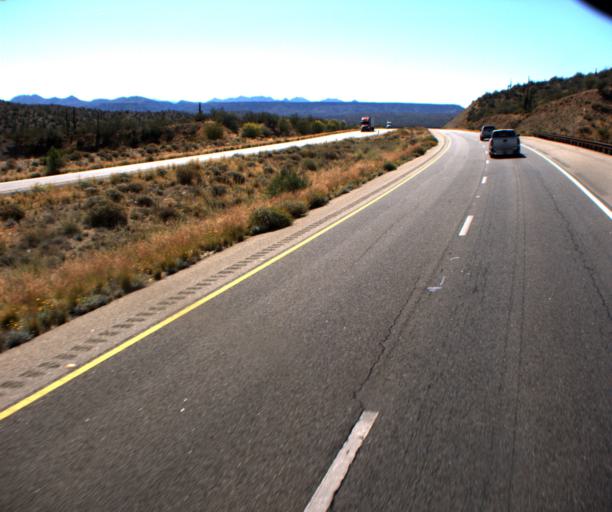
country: US
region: Arizona
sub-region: Yavapai County
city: Bagdad
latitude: 34.3892
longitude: -113.2073
